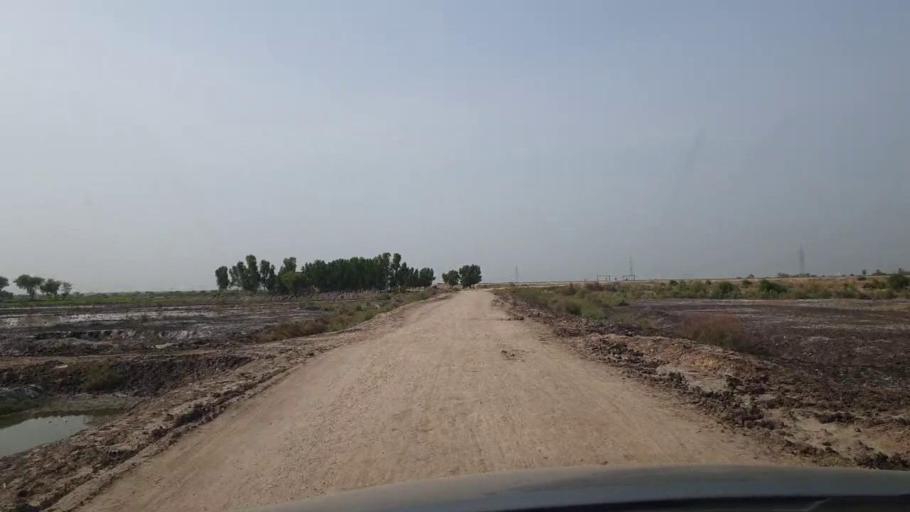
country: PK
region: Sindh
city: Lakhi
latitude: 27.8353
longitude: 68.6998
